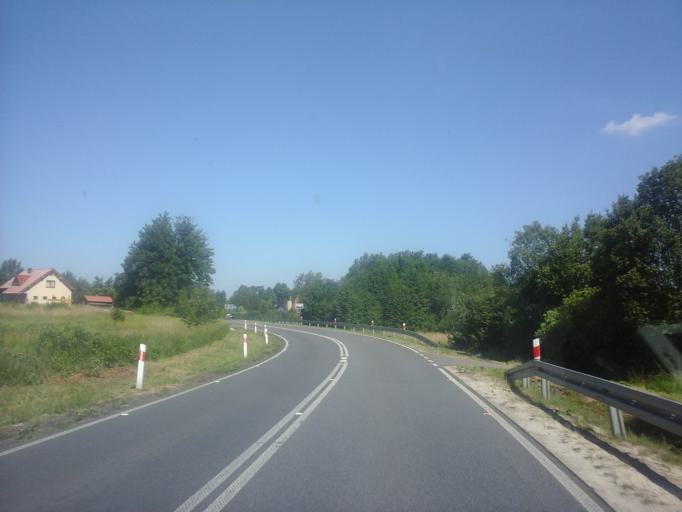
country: PL
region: West Pomeranian Voivodeship
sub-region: Koszalin
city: Koszalin
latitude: 54.1164
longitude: 16.1690
